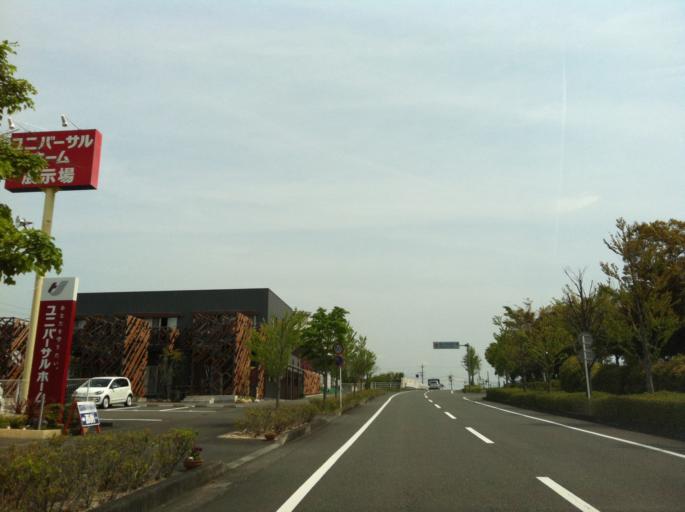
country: JP
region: Shizuoka
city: Kakegawa
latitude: 34.7702
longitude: 137.9973
